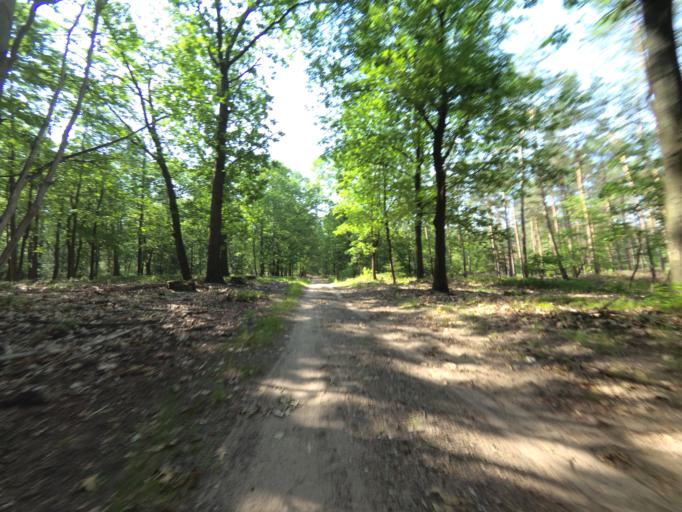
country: NL
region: Gelderland
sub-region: Gemeente Apeldoorn
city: Beekbergen
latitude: 52.1406
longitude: 5.9368
